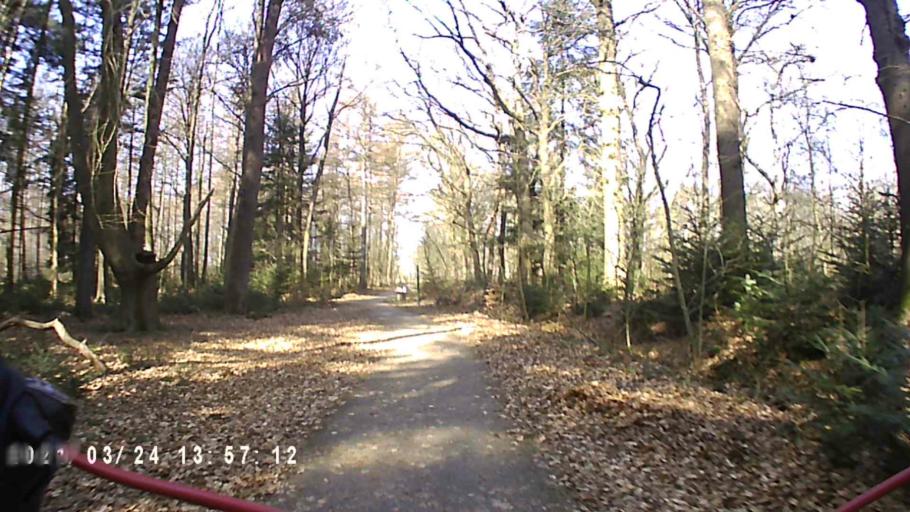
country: NL
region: Friesland
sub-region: Gemeente Smallingerland
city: Drachtstercompagnie
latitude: 53.0829
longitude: 6.2321
